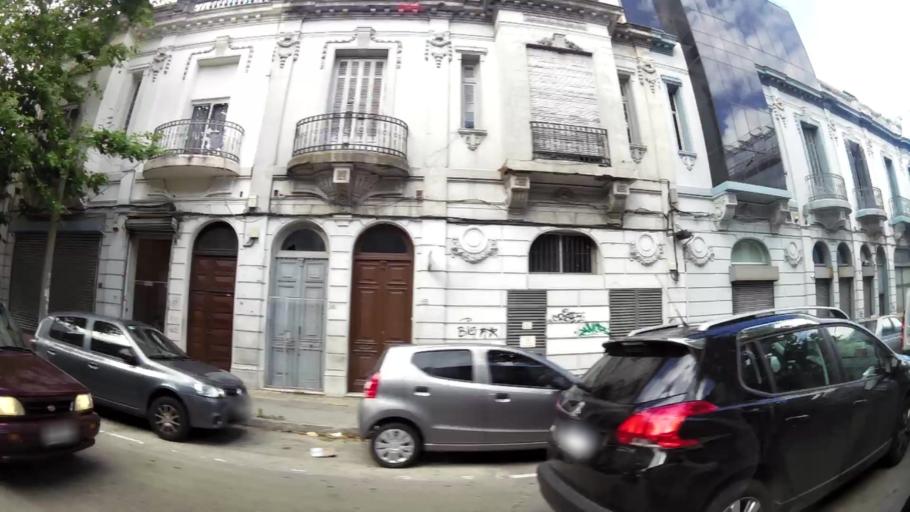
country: UY
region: Montevideo
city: Montevideo
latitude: -34.8944
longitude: -56.1837
